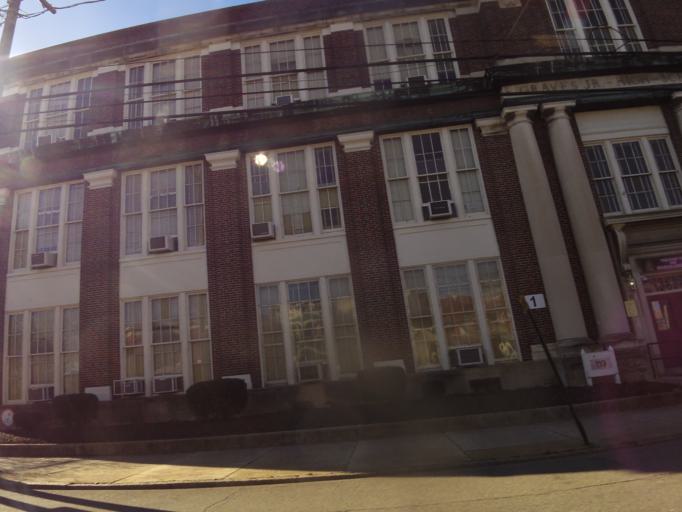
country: US
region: Virginia
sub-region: City of Richmond
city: Richmond
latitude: 37.5495
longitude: -77.4408
